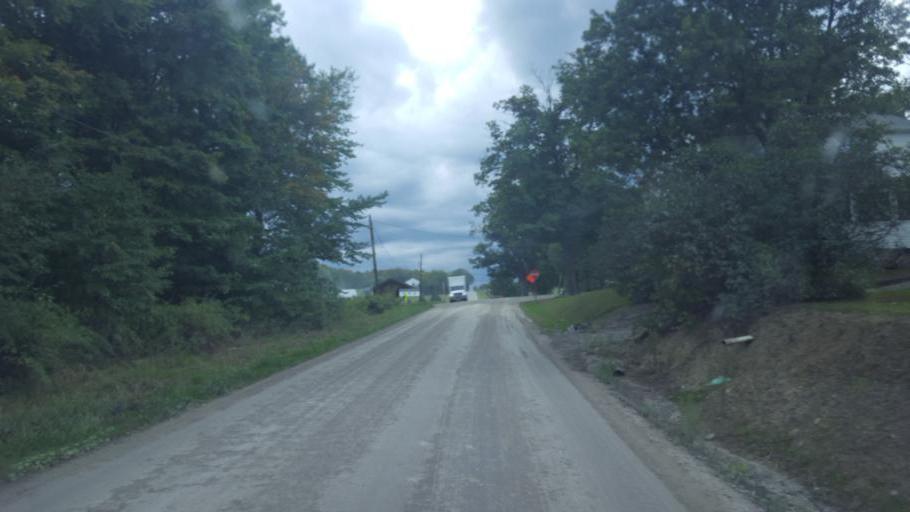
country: US
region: Ohio
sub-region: Geauga County
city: Middlefield
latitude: 41.3864
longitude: -81.0793
